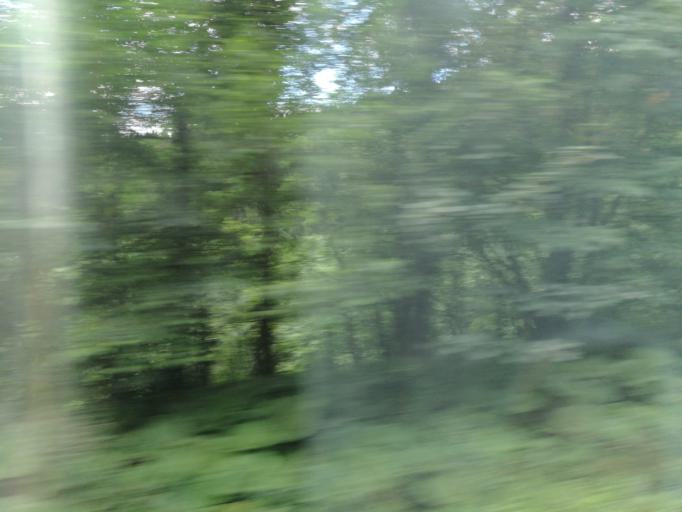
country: RO
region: Brasov
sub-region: Oras Predeal
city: Predeal
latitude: 45.5207
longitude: 25.5942
